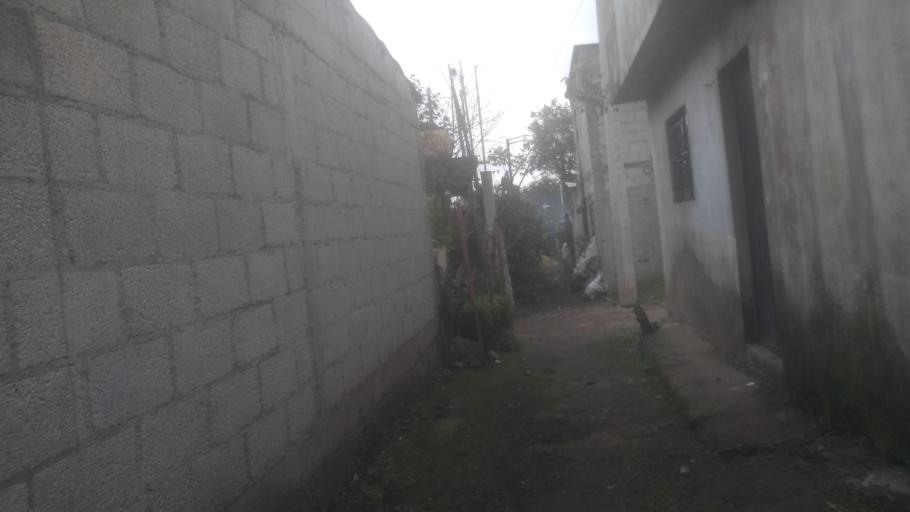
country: MX
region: Veracruz
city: Chocaman
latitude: 18.9972
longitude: -97.0445
